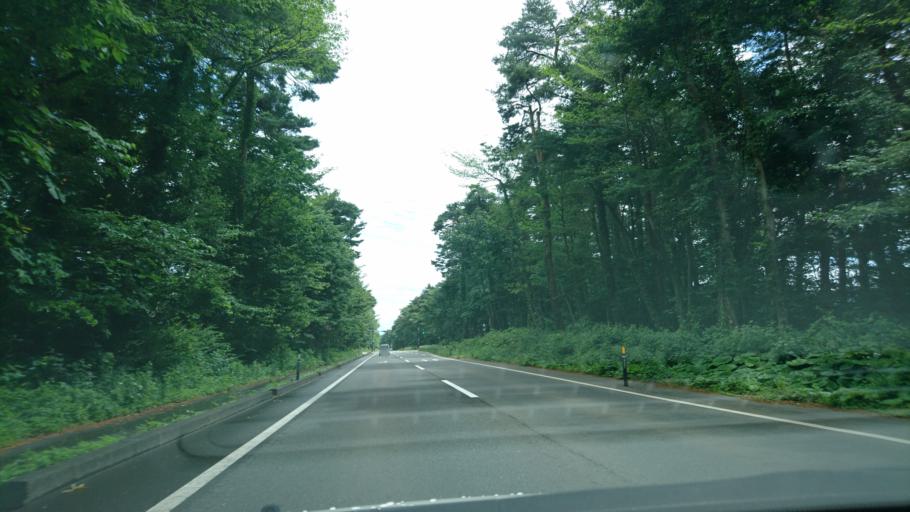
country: JP
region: Iwate
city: Morioka-shi
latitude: 39.7843
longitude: 141.1252
